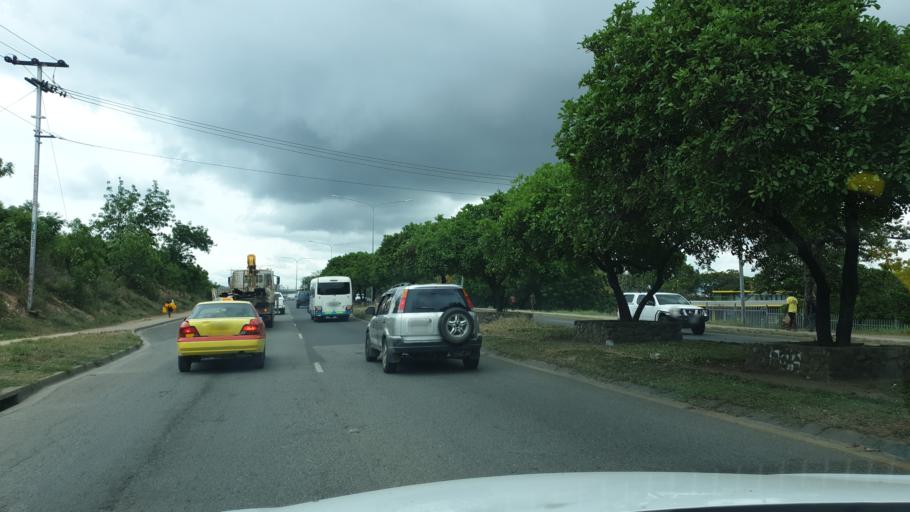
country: PG
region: National Capital
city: Port Moresby
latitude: -9.4580
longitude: 147.1913
